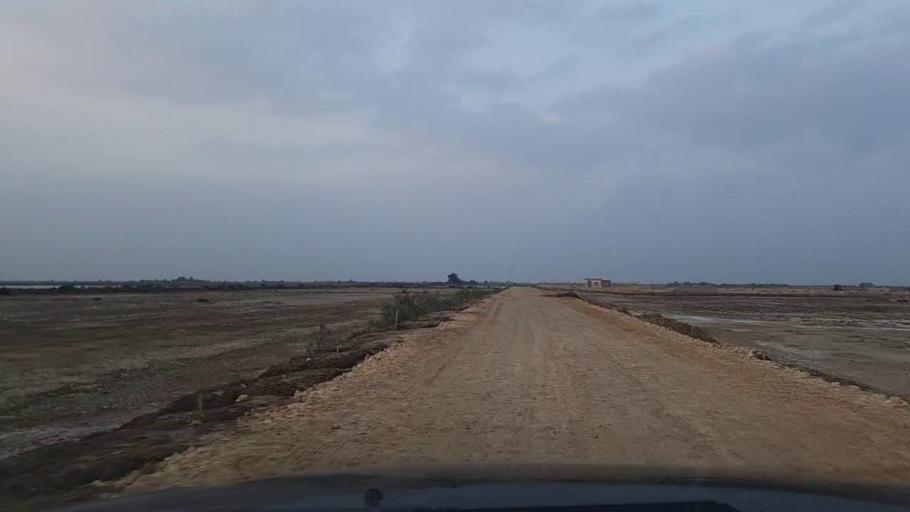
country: PK
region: Sindh
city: Jati
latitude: 24.4919
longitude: 68.3918
